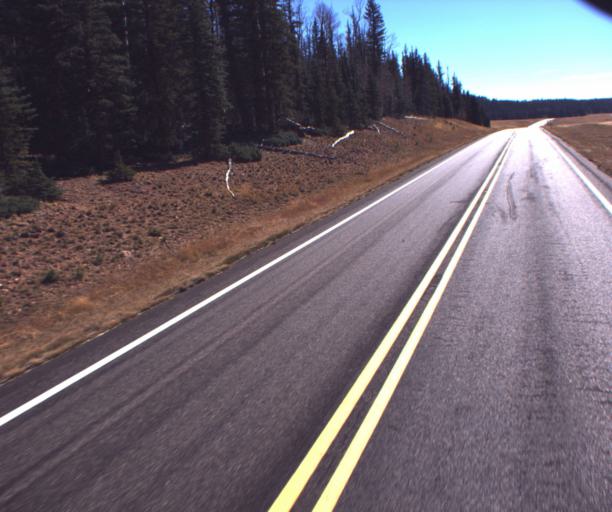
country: US
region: Arizona
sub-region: Coconino County
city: Grand Canyon
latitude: 36.3735
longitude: -112.1240
